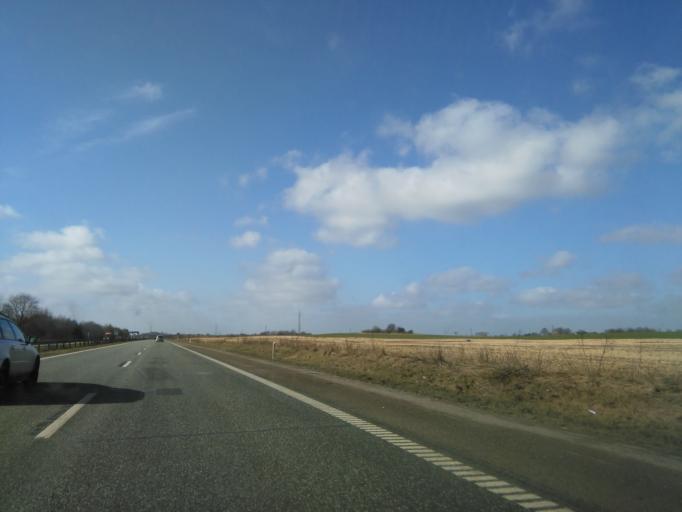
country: DK
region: Zealand
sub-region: Koge Kommune
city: Ejby
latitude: 55.4796
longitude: 12.1277
